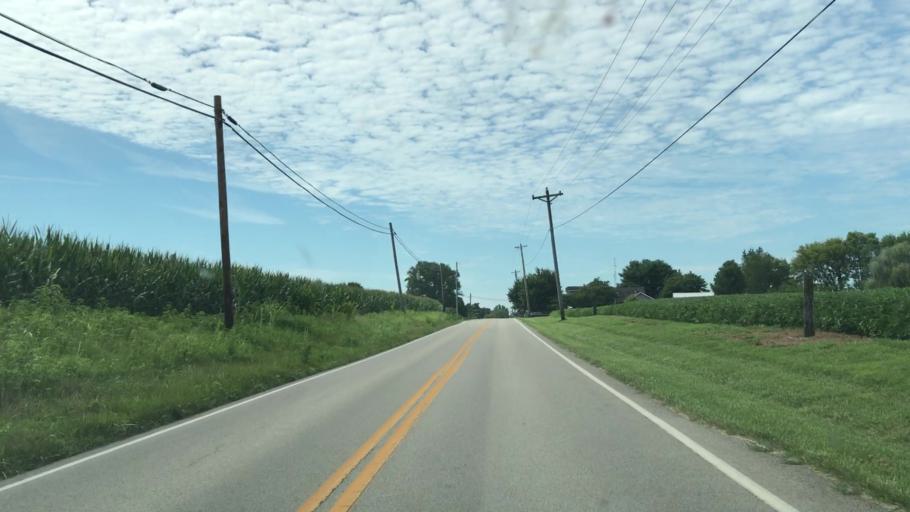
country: US
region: Kentucky
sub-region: Edmonson County
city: Brownsville
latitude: 37.0696
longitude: -86.2115
